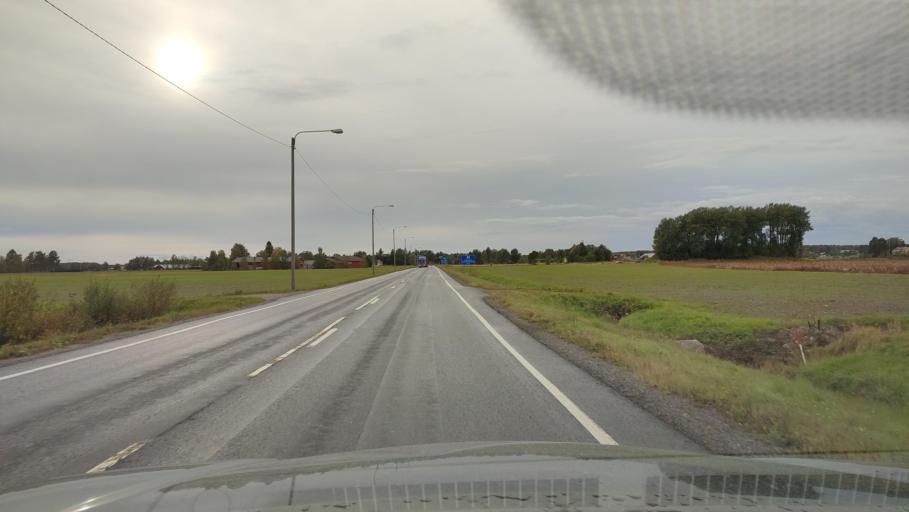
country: FI
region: Ostrobothnia
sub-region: Sydosterbotten
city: Kristinestad
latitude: 62.2605
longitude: 21.5039
